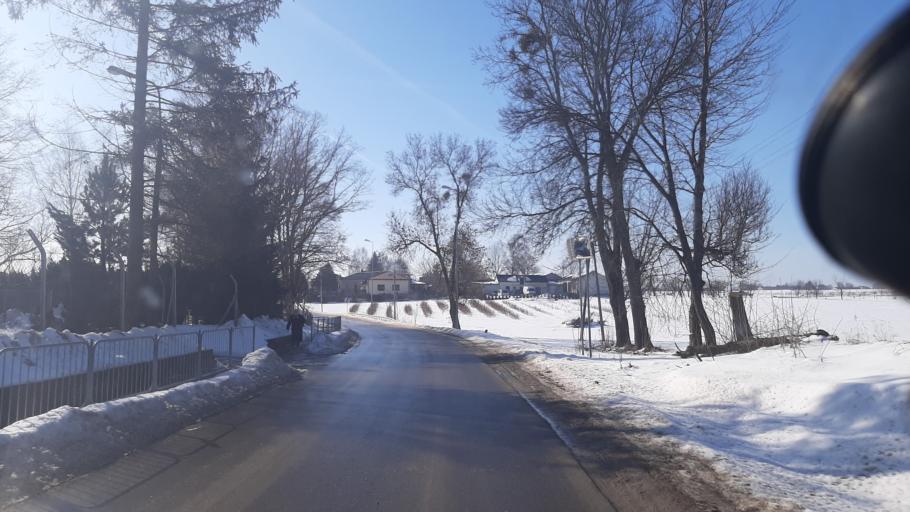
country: PL
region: Lublin Voivodeship
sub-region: Powiat lubelski
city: Garbow
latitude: 51.3124
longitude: 22.3081
